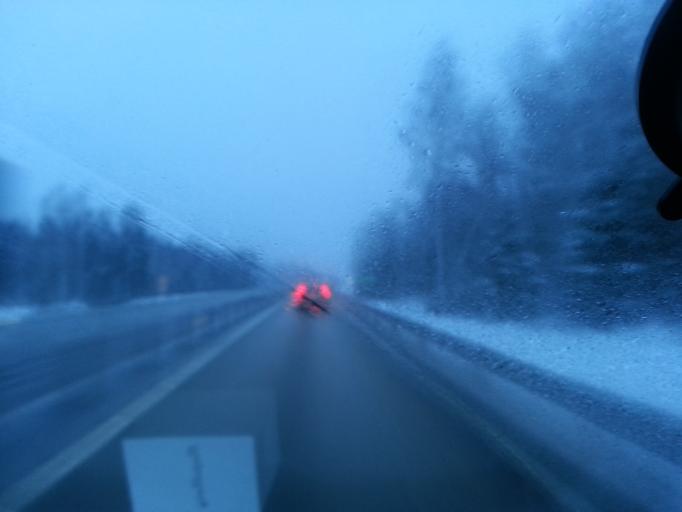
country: SE
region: Kronoberg
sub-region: Ljungby Kommun
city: Lagan
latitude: 57.0178
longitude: 14.0404
